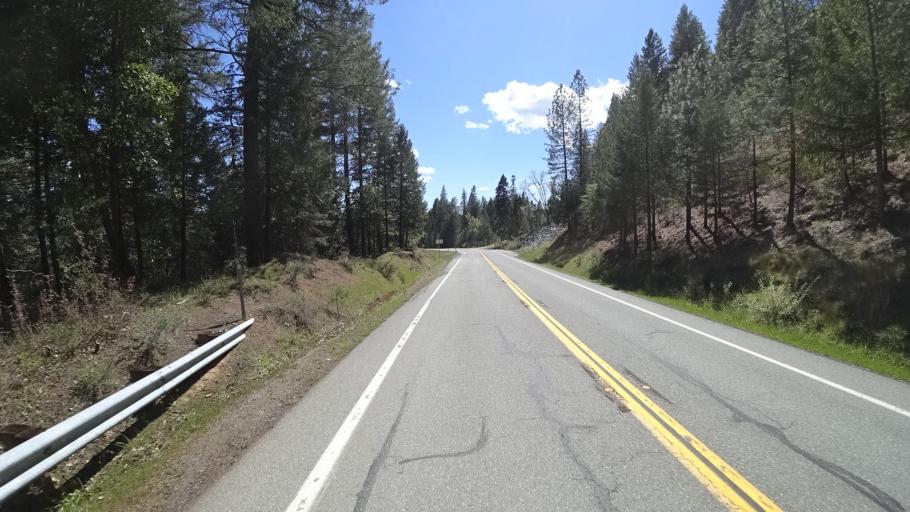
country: US
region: California
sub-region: Trinity County
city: Lewiston
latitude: 40.8689
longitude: -122.8032
